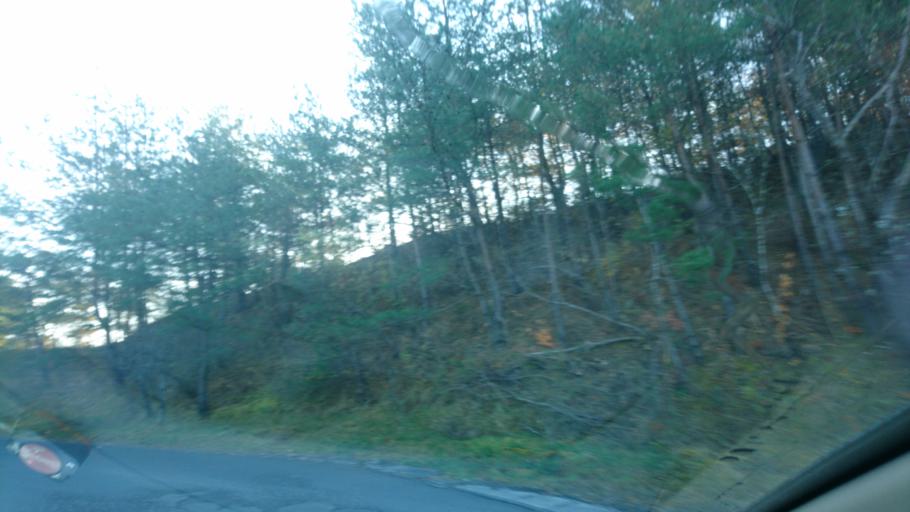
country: JP
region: Iwate
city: Ichinoseki
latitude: 38.9015
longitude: 141.1520
